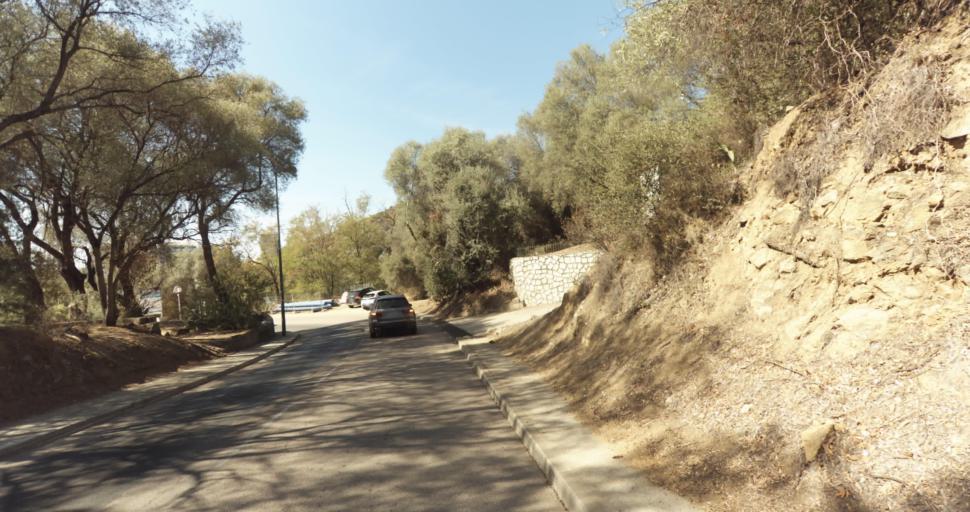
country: FR
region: Corsica
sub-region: Departement de la Corse-du-Sud
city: Ajaccio
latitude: 41.9171
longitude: 8.7232
